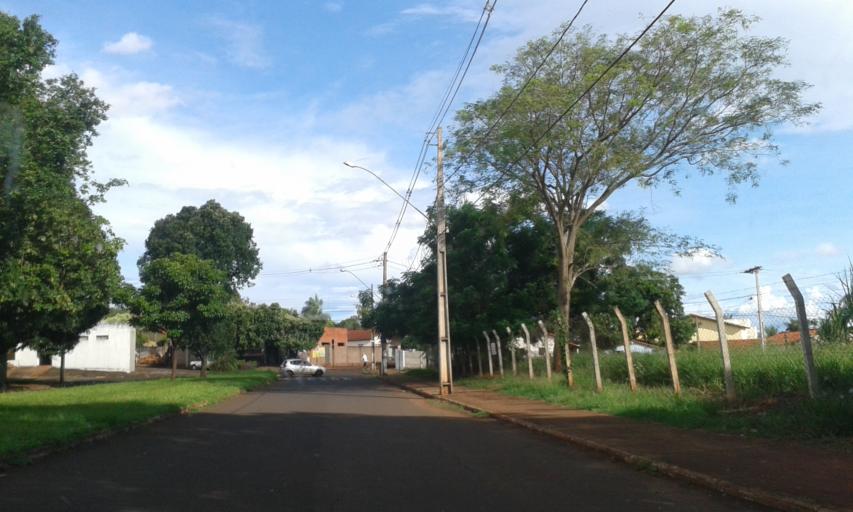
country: BR
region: Minas Gerais
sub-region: Ituiutaba
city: Ituiutaba
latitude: -18.9733
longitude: -49.4451
